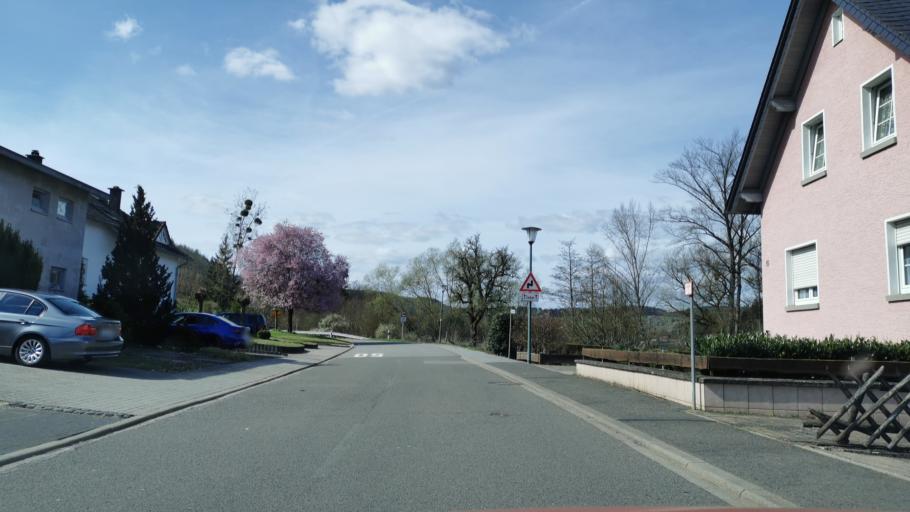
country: DE
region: Rheinland-Pfalz
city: Dreis
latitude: 49.9280
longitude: 6.8297
